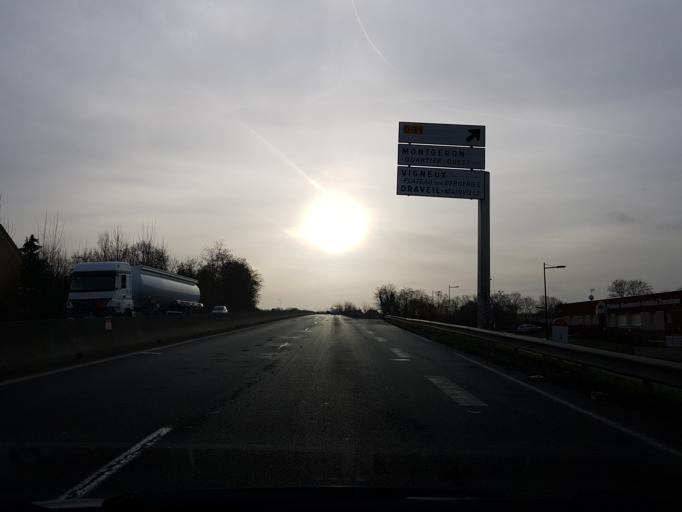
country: FR
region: Ile-de-France
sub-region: Departement de l'Essonne
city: Montgeron
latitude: 48.6954
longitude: 2.4464
